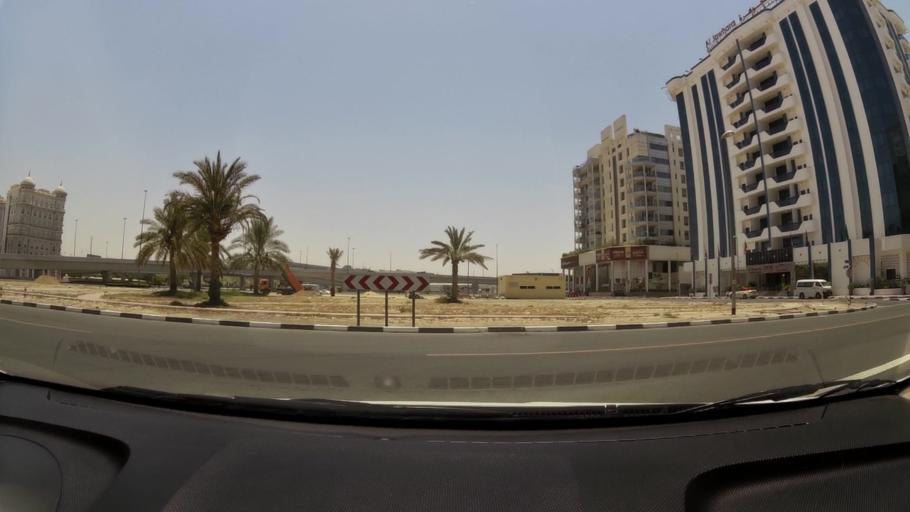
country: AE
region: Ash Shariqah
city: Sharjah
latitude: 25.2557
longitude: 55.3350
